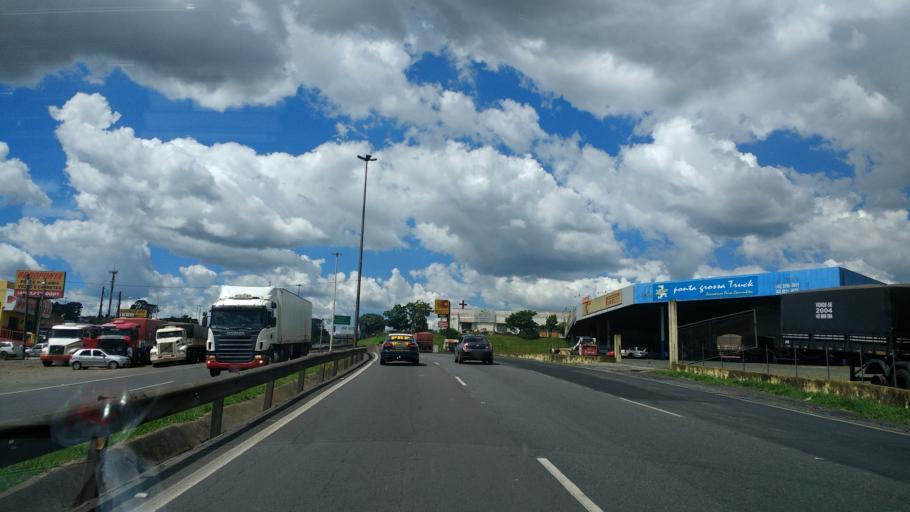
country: BR
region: Parana
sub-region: Ponta Grossa
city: Ponta Grossa
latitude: -25.0857
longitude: -50.1921
